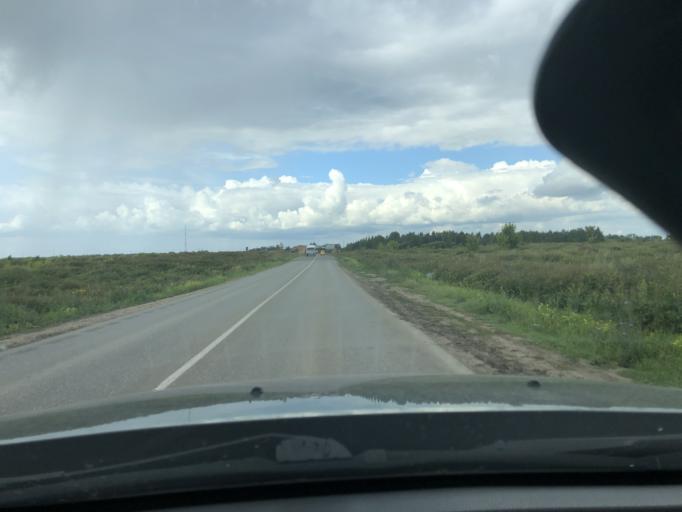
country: RU
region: Tula
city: Kamenetskiy
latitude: 54.0129
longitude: 38.2509
